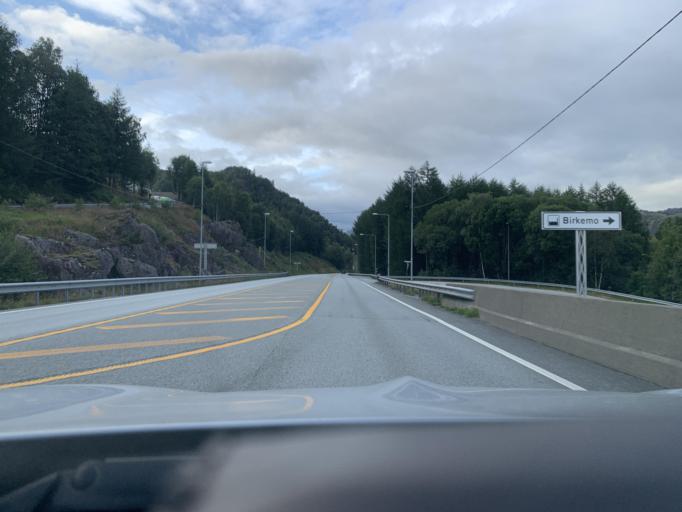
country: NO
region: Rogaland
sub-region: Bjerkreim
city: Vikesa
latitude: 58.5941
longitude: 6.0790
